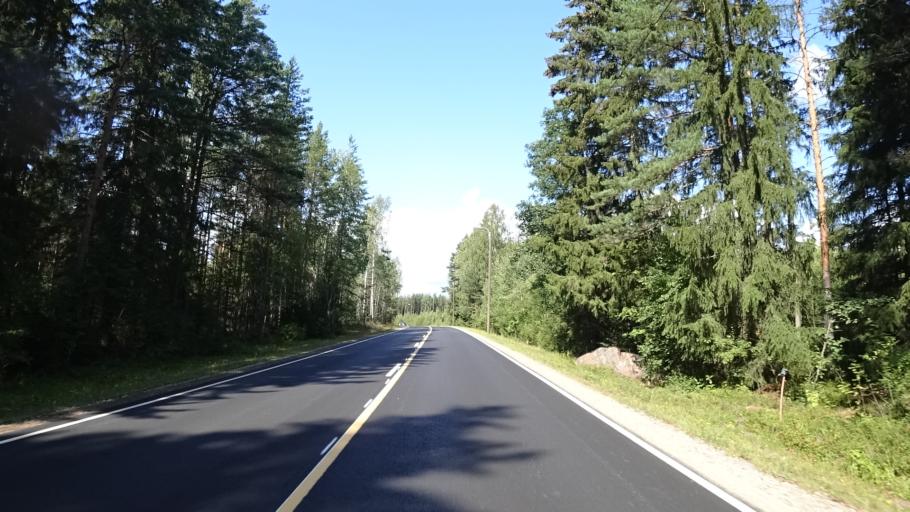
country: FI
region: Kymenlaakso
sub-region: Kotka-Hamina
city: Karhula
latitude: 60.5505
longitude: 26.9094
